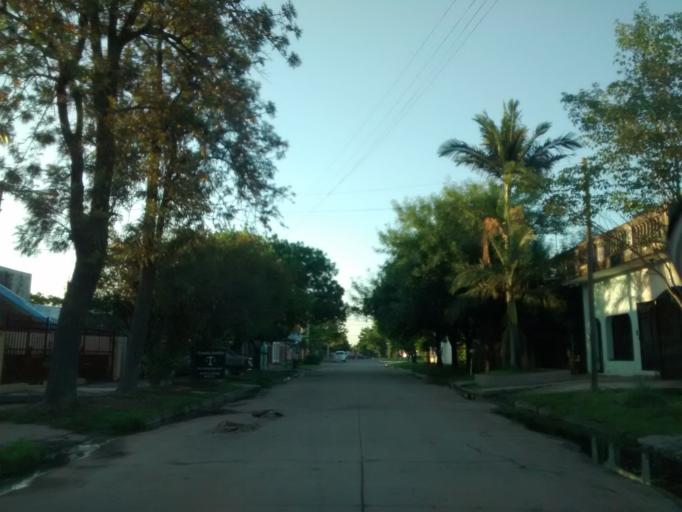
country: AR
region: Chaco
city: Barranqueras
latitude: -27.4839
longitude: -58.9444
